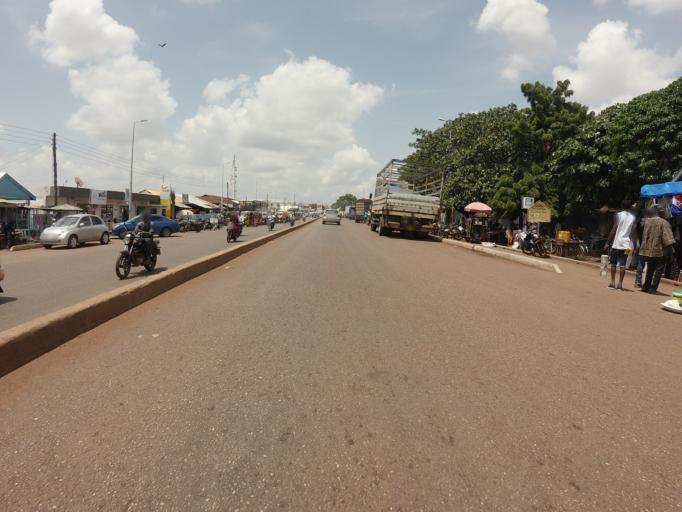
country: GH
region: Northern
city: Tamale
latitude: 9.4043
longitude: -0.8490
